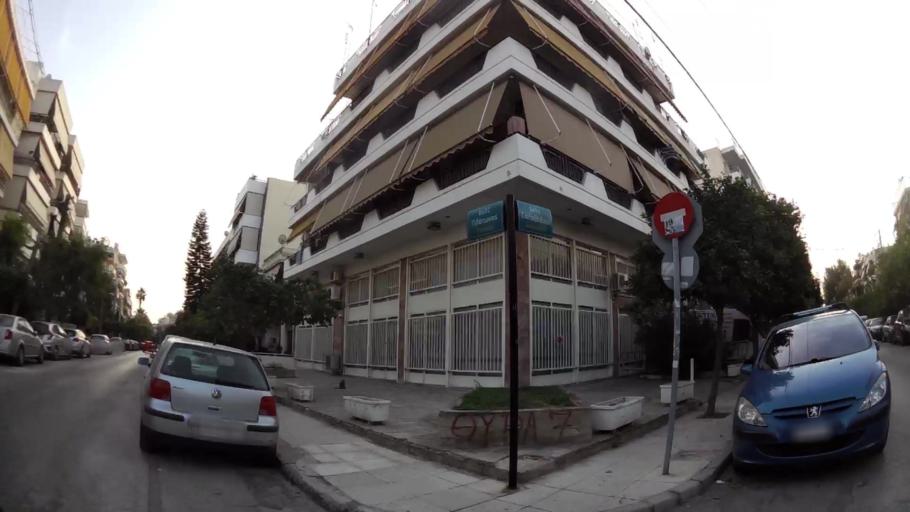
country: GR
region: Attica
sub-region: Nomarchia Athinas
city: Moskhaton
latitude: 37.9543
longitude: 23.6846
